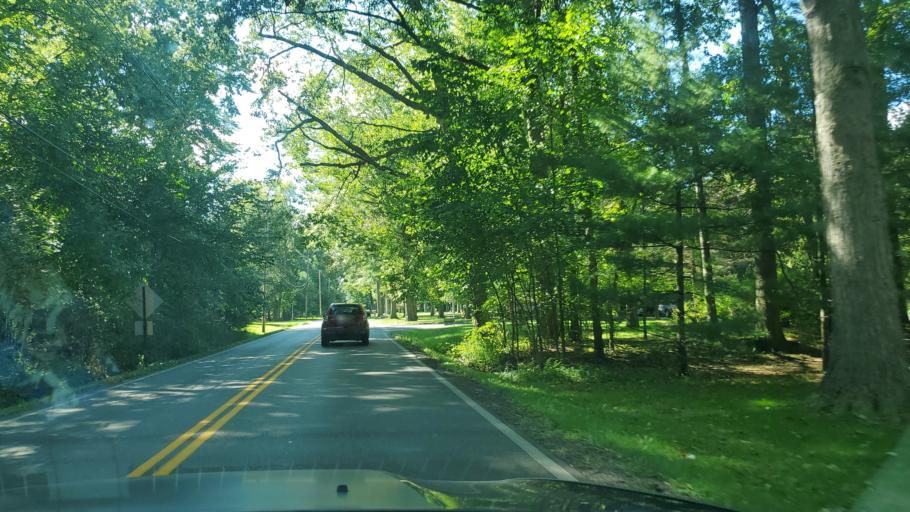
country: US
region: Ohio
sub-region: Mahoning County
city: Boardman
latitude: 41.0466
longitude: -80.6859
